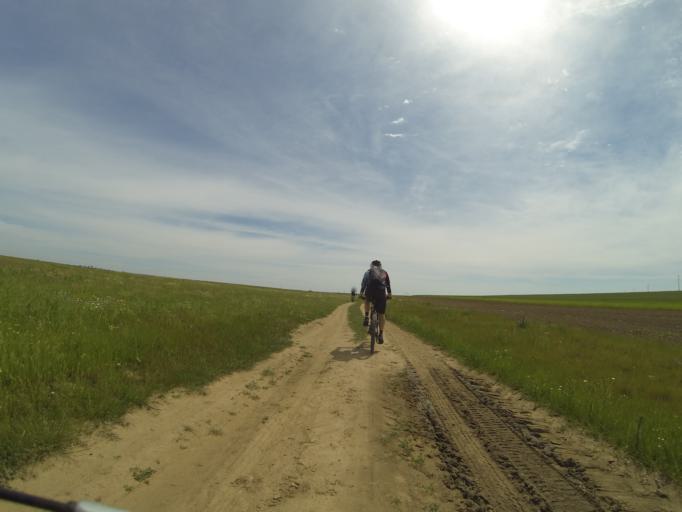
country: RO
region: Dolj
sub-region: Comuna Ghindeni
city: Ghindeni
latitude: 44.2069
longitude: 23.9502
